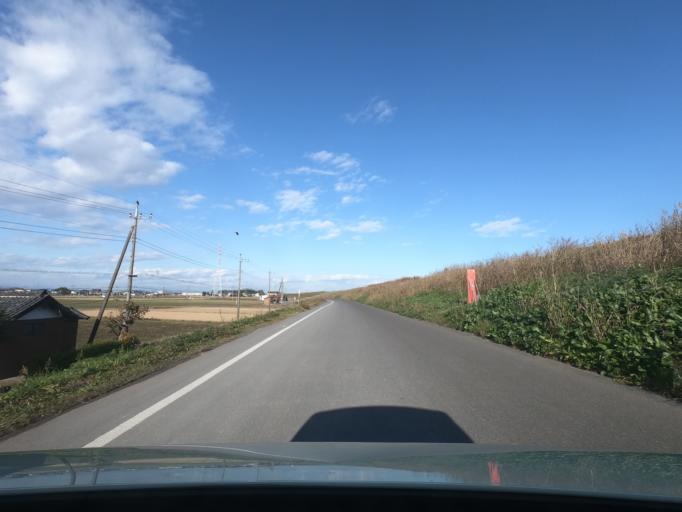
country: JP
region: Ibaraki
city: Koga
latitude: 36.2495
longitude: 139.7343
